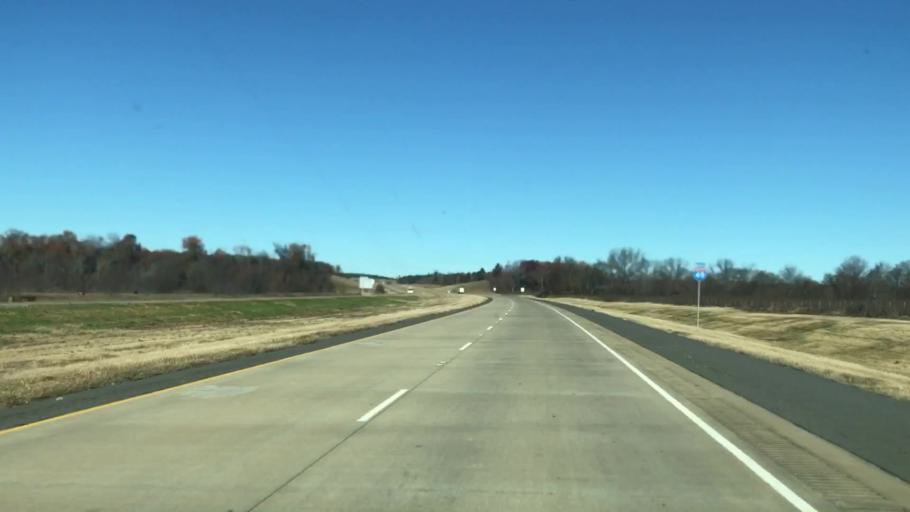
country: US
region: Louisiana
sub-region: Caddo Parish
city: Vivian
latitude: 32.9069
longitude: -93.8669
